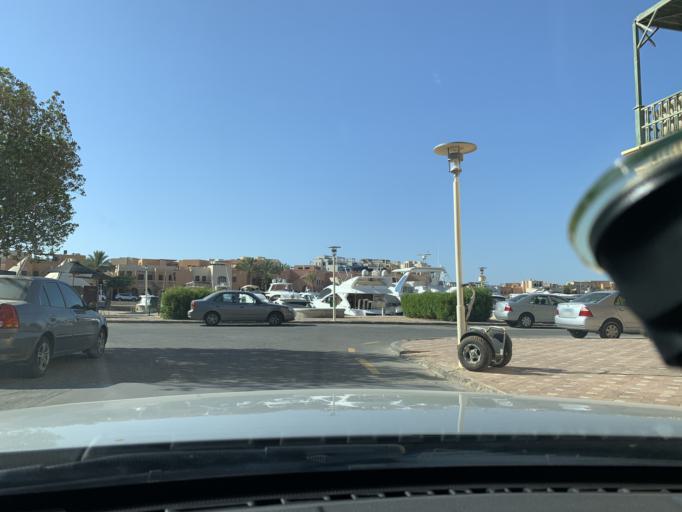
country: EG
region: Red Sea
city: El Gouna
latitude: 27.4068
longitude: 33.6750
